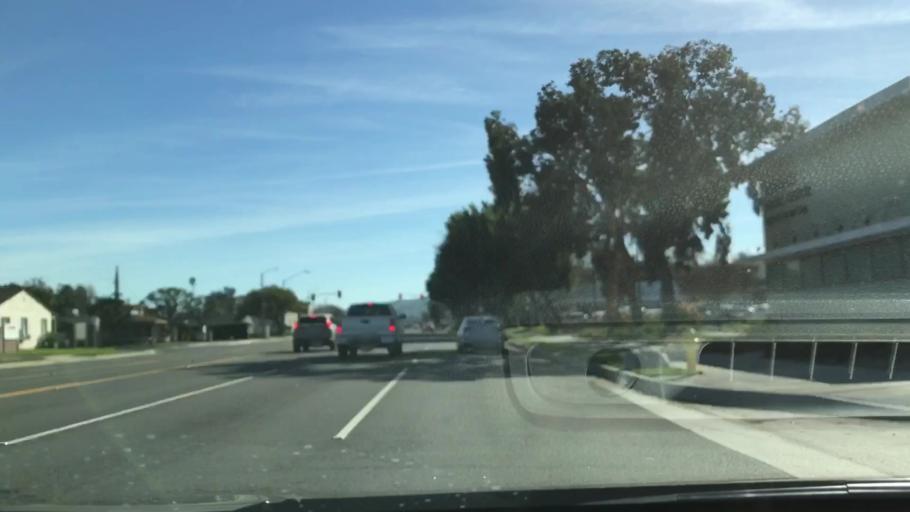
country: US
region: California
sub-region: Los Angeles County
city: Lomita
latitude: 33.8113
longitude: -118.3282
